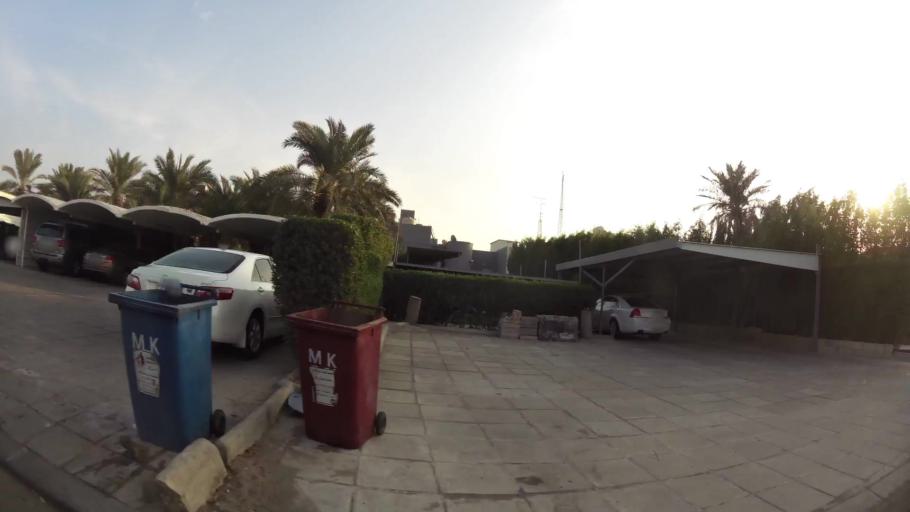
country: KW
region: Mubarak al Kabir
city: Sabah as Salim
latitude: 29.2576
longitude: 48.0735
